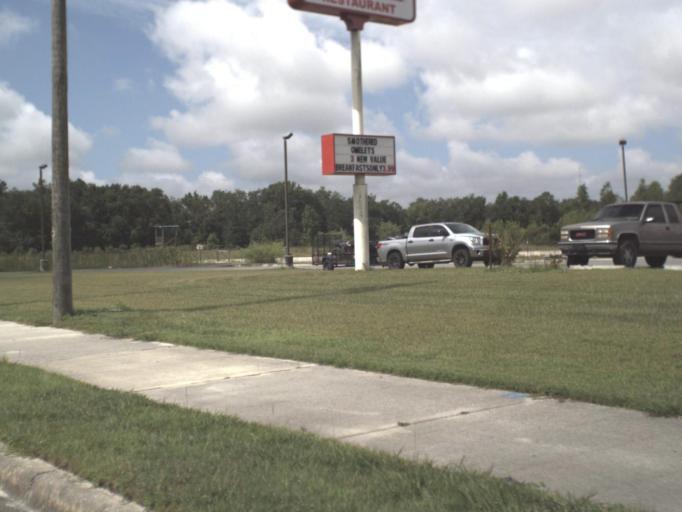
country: US
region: Florida
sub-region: Columbia County
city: Five Points
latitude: 30.2361
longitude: -82.6387
